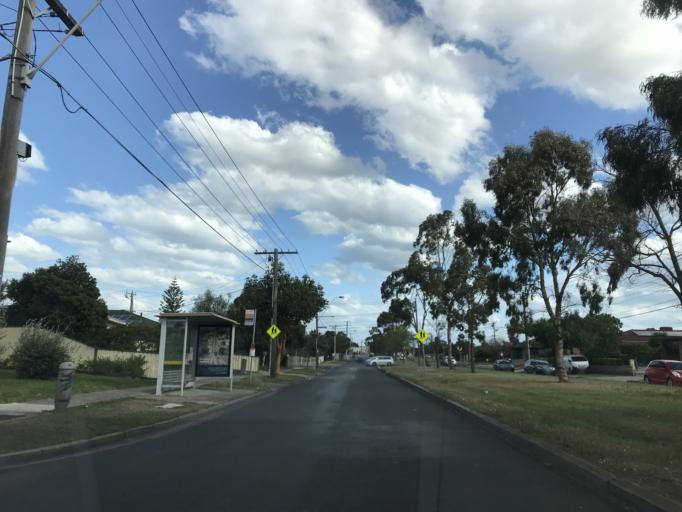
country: AU
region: Victoria
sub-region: Brimbank
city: Sunshine West
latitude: -37.8012
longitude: 144.8187
